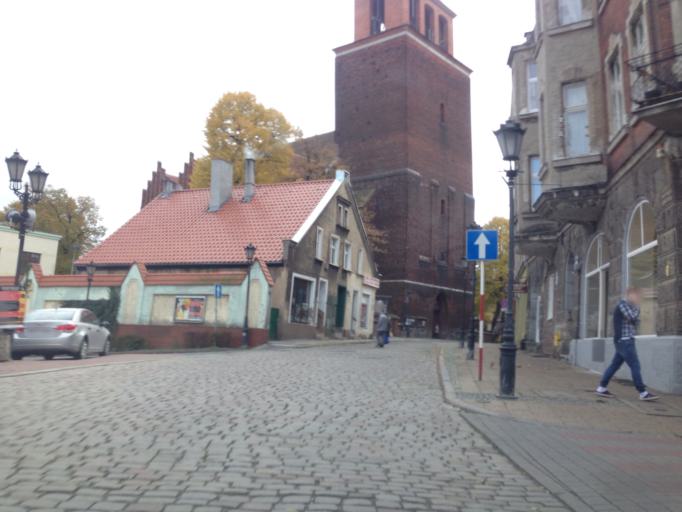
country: PL
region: Pomeranian Voivodeship
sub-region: Powiat tczewski
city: Tczew
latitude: 54.0885
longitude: 18.7987
